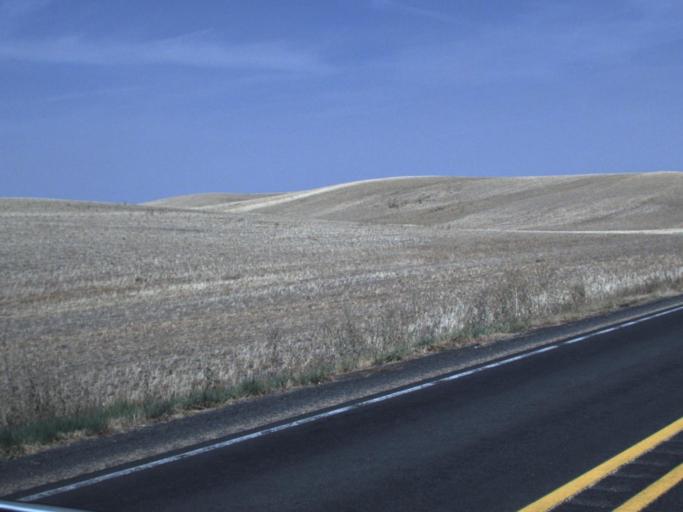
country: US
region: Washington
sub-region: Whitman County
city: Colfax
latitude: 47.1517
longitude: -117.2327
